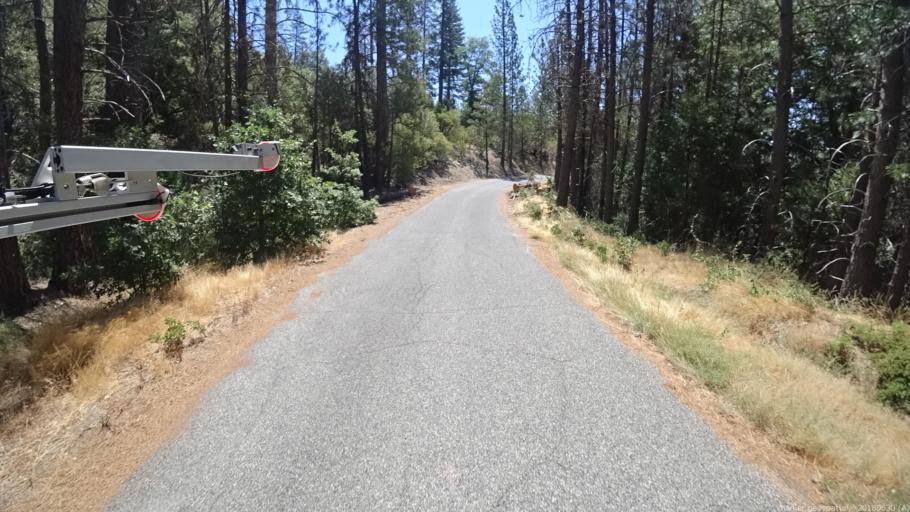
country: US
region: California
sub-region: Madera County
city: Oakhurst
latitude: 37.3599
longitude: -119.3473
